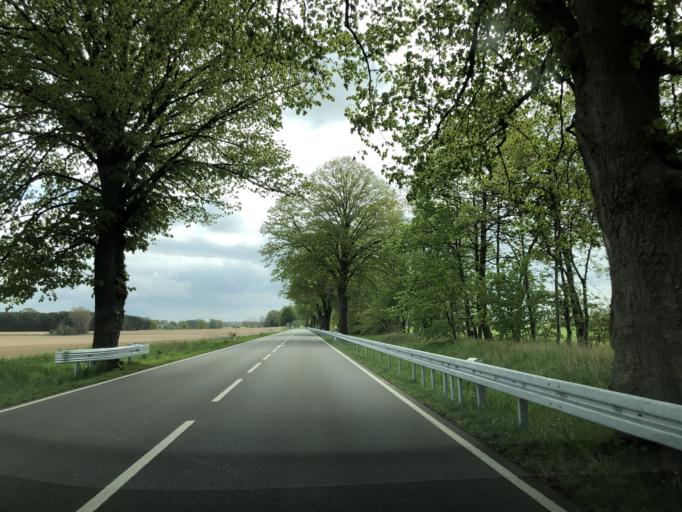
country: DE
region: Mecklenburg-Vorpommern
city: Lubz
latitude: 53.4635
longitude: 12.1433
